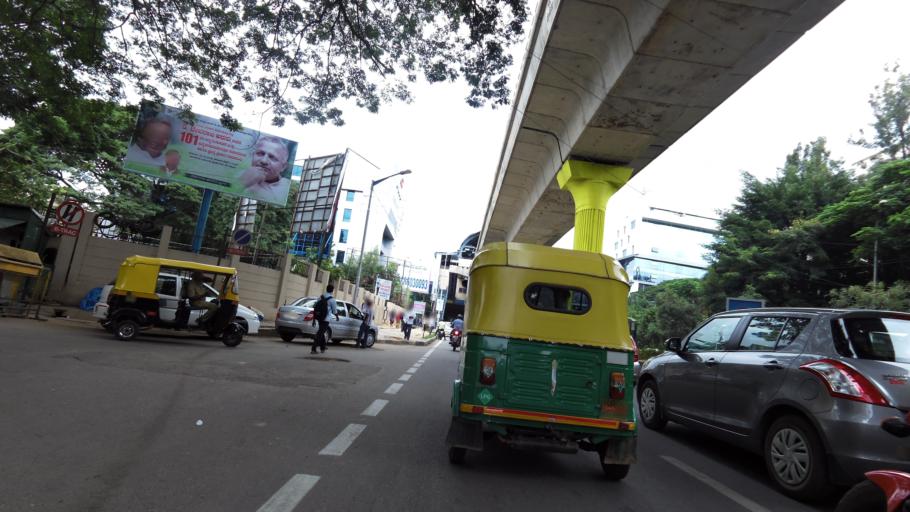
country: IN
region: Karnataka
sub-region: Bangalore Urban
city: Bangalore
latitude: 12.9726
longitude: 77.6185
